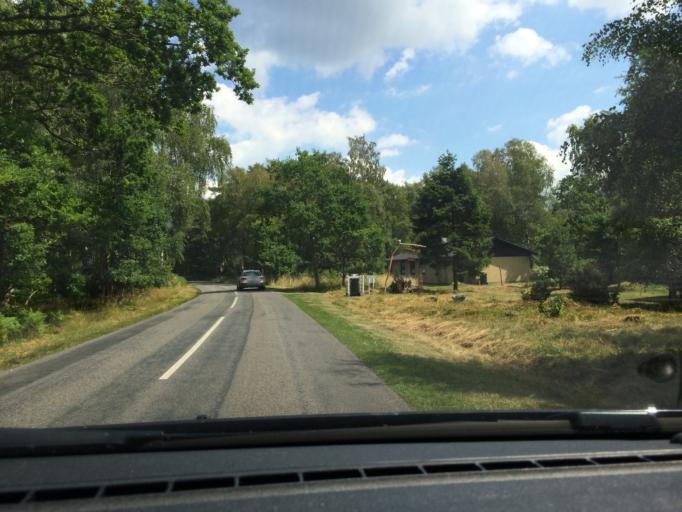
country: DK
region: Zealand
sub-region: Vordingborg Kommune
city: Stege
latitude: 55.0486
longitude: 12.2453
